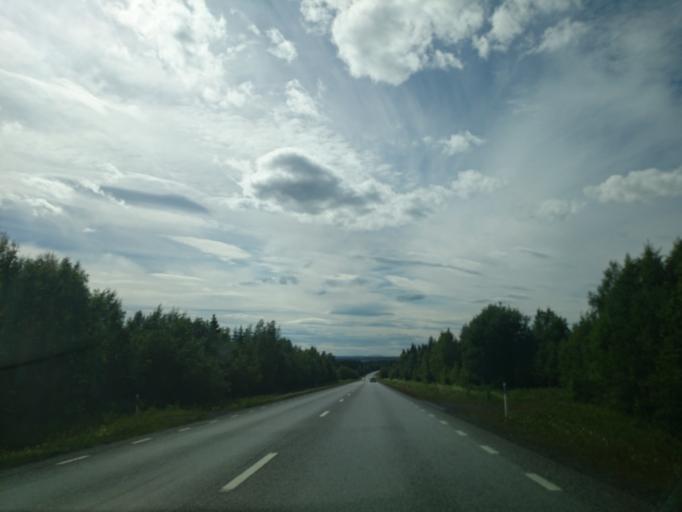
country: SE
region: Jaemtland
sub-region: Krokoms Kommun
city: Valla
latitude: 63.3066
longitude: 13.8539
